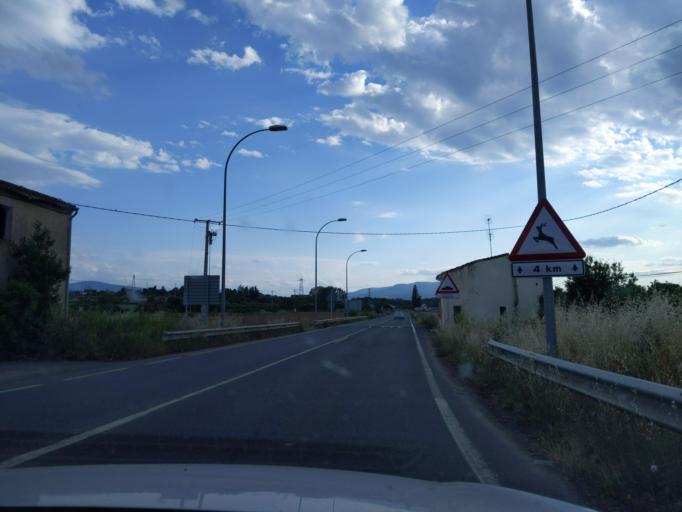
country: ES
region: La Rioja
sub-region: Provincia de La Rioja
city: Villamediana de Iregua
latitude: 42.4231
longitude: -2.4249
